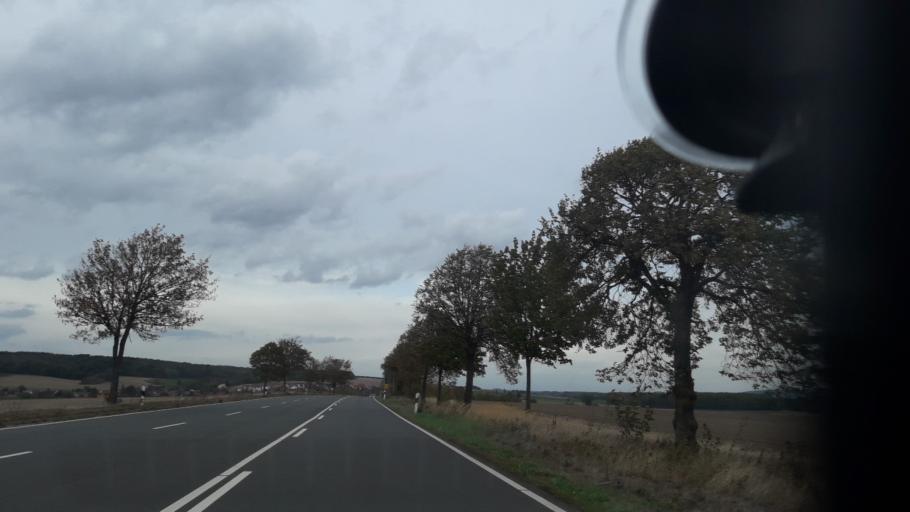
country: DE
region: Lower Saxony
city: Werlaburgdorf
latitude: 52.0407
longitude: 10.5404
